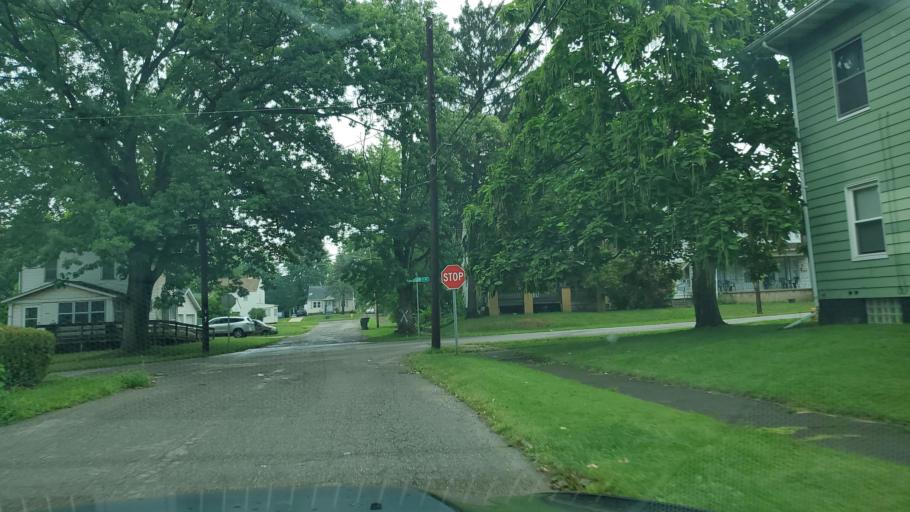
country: US
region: Ohio
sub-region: Trumbull County
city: Warren
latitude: 41.2390
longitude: -80.8044
